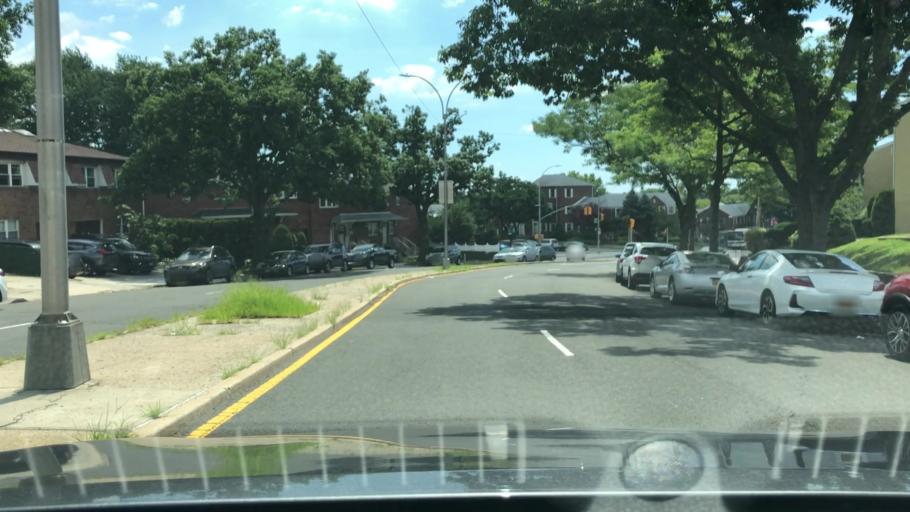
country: US
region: New York
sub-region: Nassau County
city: Lake Success
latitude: 40.7529
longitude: -73.7218
